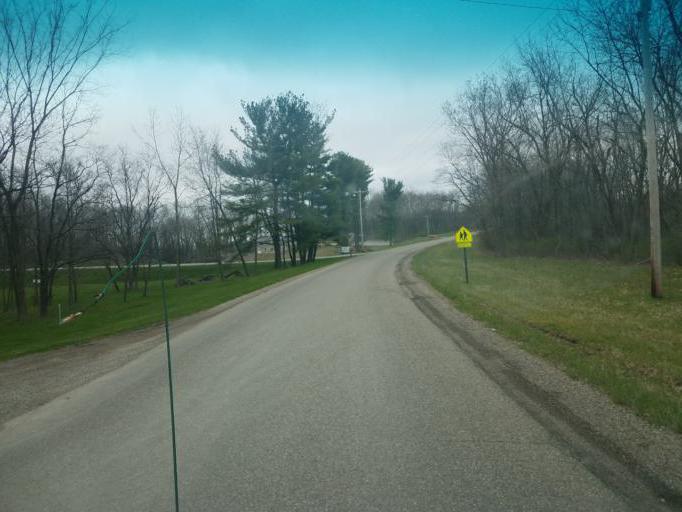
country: US
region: Ohio
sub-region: Stark County
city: Beach City
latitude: 40.6325
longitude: -81.6404
